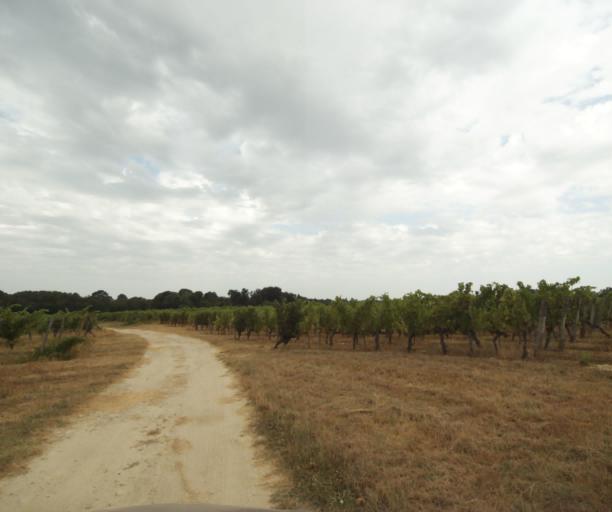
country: FR
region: Aquitaine
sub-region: Departement de la Gironde
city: La Sauve
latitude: 44.7594
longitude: -0.3324
